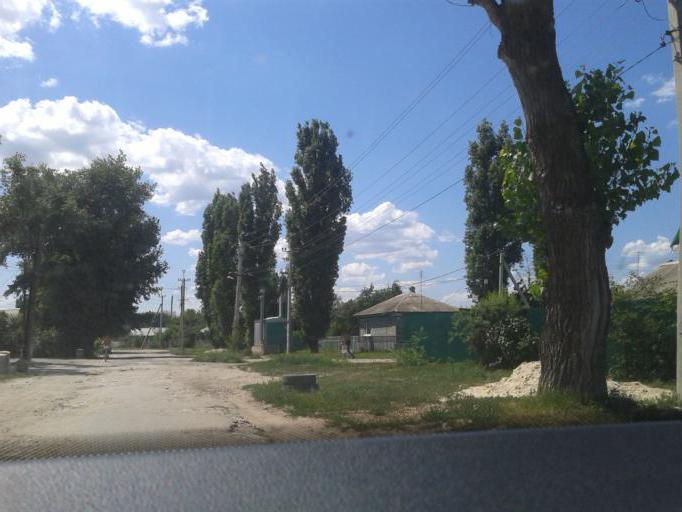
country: RU
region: Volgograd
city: Frolovo
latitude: 49.7602
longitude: 43.6626
